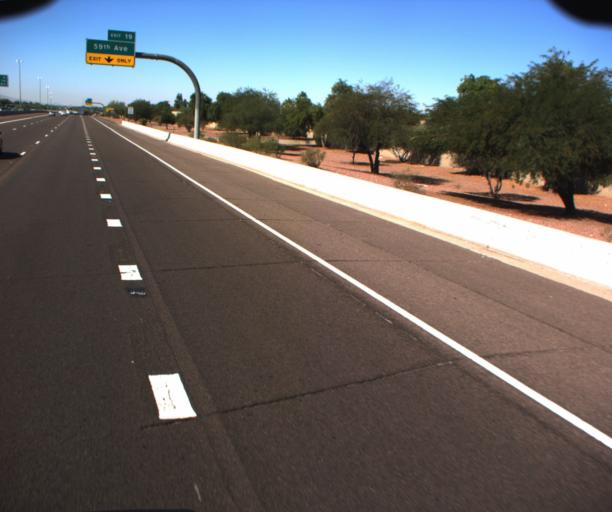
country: US
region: Arizona
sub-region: Maricopa County
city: Peoria
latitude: 33.6685
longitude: -112.1768
